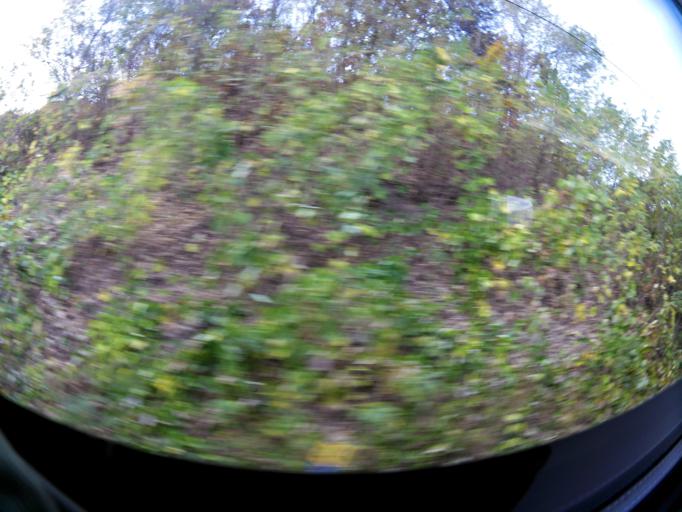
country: KR
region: Gyeongsangbuk-do
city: Gimcheon
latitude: 36.1707
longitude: 128.0062
